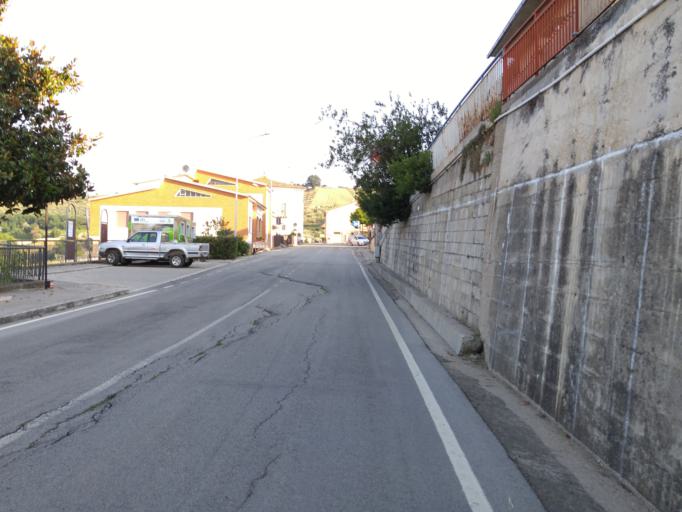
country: IT
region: Abruzzo
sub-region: Provincia di Teramo
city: Castilenti
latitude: 42.5604
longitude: 13.9220
